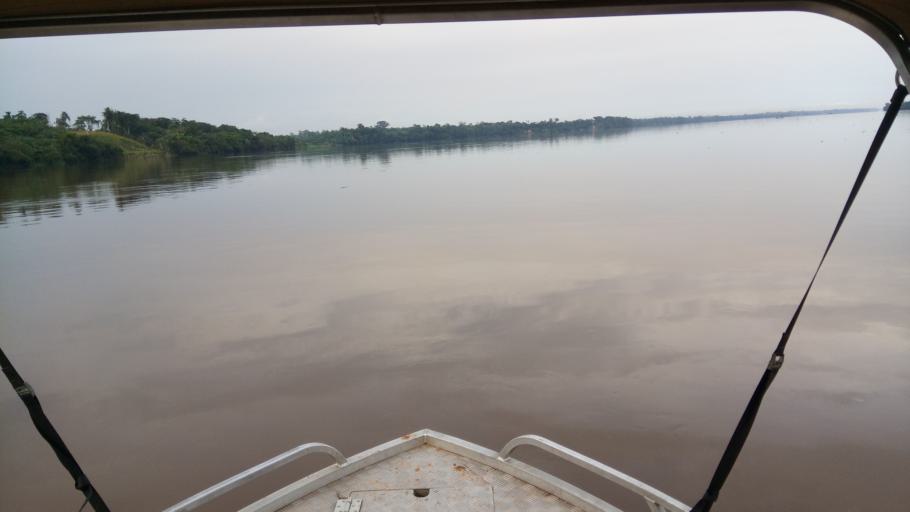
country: CD
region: Eastern Province
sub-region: Sous-Region de la Tshopo
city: Yangambi
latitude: 0.5725
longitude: 24.7804
